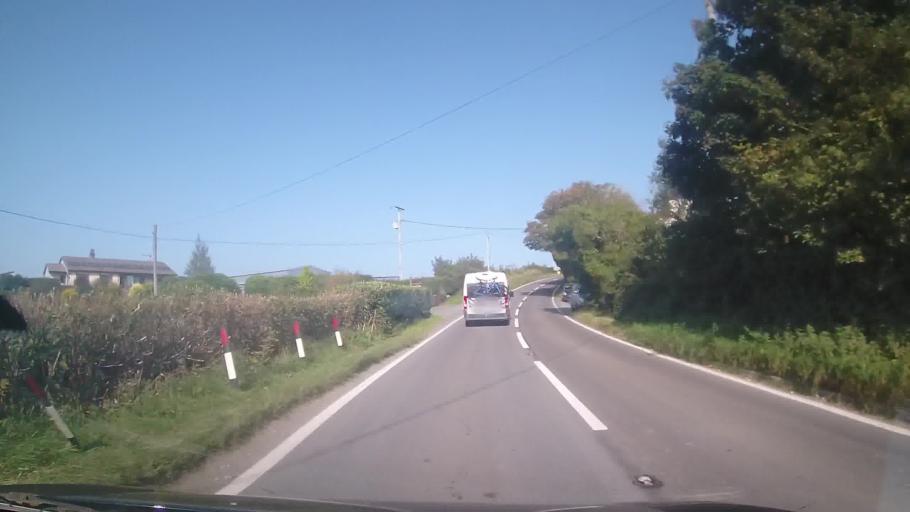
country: GB
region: Wales
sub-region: County of Ceredigion
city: Cardigan
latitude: 52.0670
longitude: -4.6798
